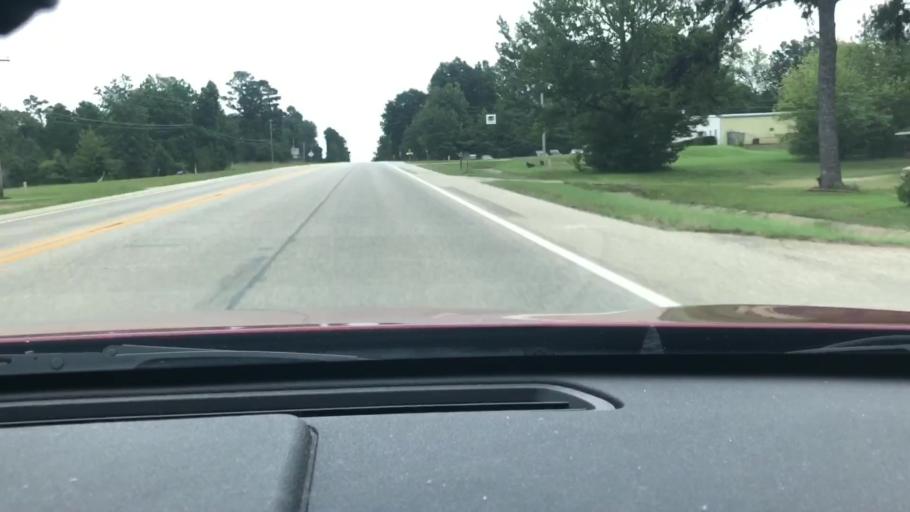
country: US
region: Arkansas
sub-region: Miller County
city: Texarkana
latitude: 33.4294
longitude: -93.9428
